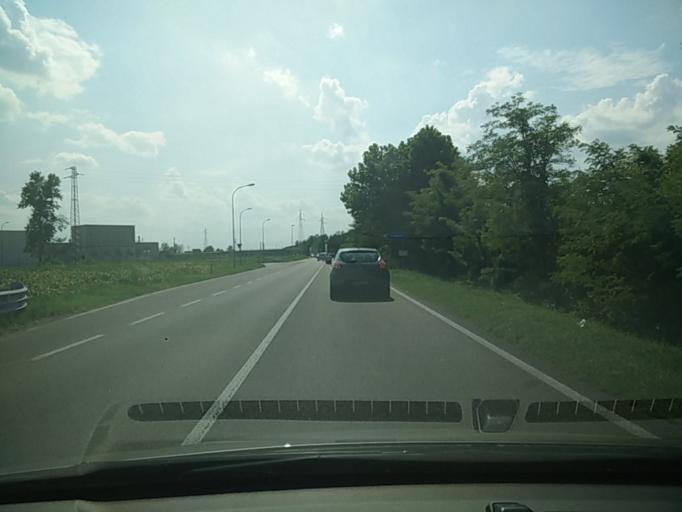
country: IT
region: Veneto
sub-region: Provincia di Treviso
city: Salvatronda
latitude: 45.6891
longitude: 11.9720
